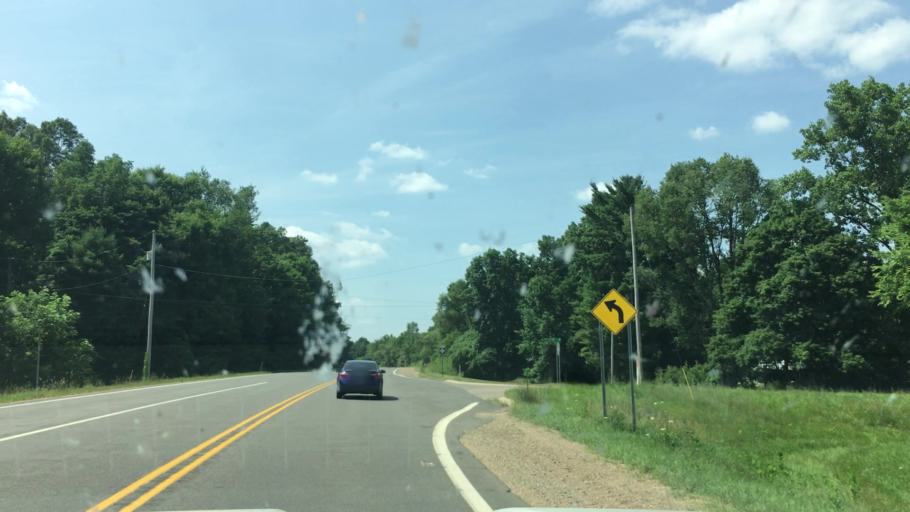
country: US
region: Michigan
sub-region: Allegan County
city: Plainwell
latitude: 42.4391
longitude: -85.5831
